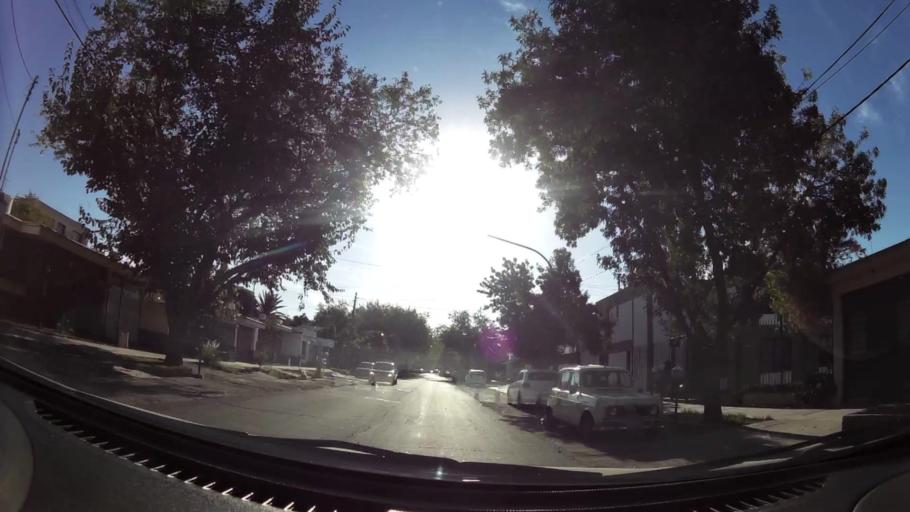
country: AR
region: Mendoza
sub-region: Departamento de Godoy Cruz
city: Godoy Cruz
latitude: -32.9134
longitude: -68.8307
